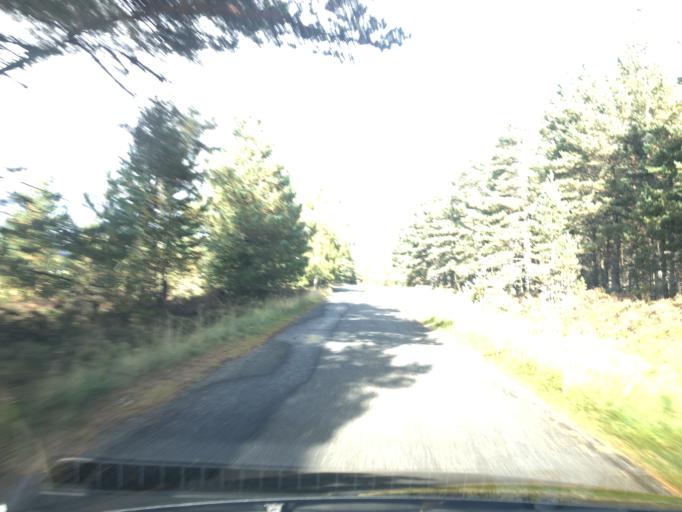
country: GB
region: Scotland
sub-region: Highland
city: Aviemore
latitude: 57.1031
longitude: -3.8897
